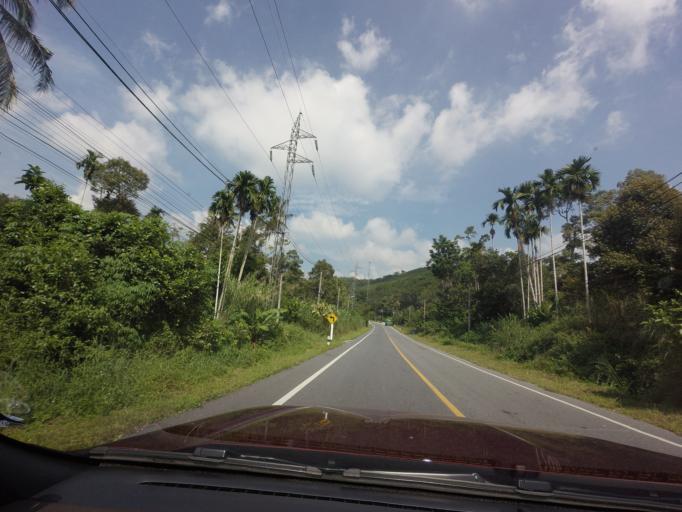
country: TH
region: Yala
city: Betong
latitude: 5.8323
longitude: 101.1149
